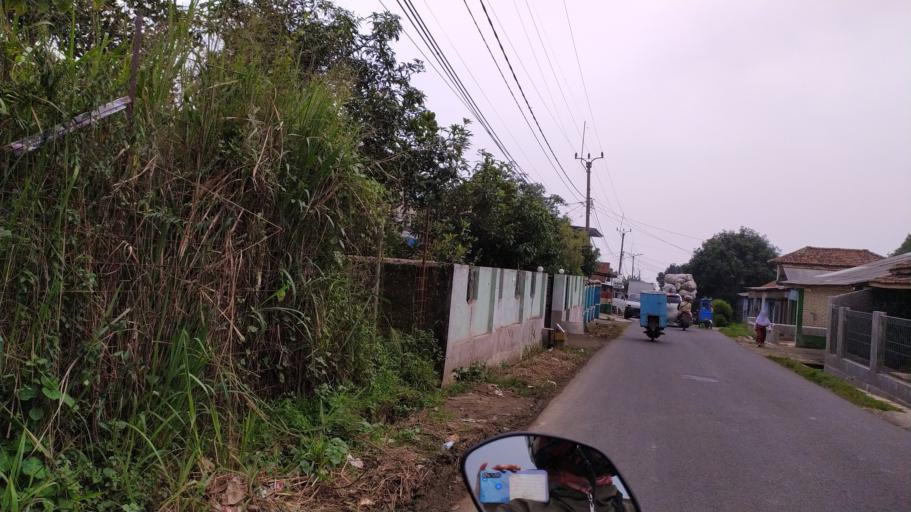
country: ID
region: West Java
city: Ciampea
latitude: -6.5988
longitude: 106.7037
